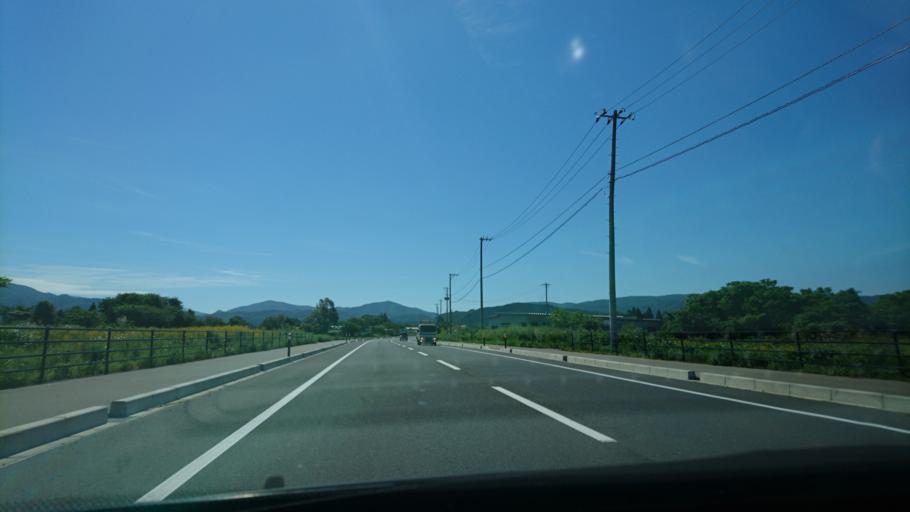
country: JP
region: Iwate
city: Tono
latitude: 39.2996
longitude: 141.5779
